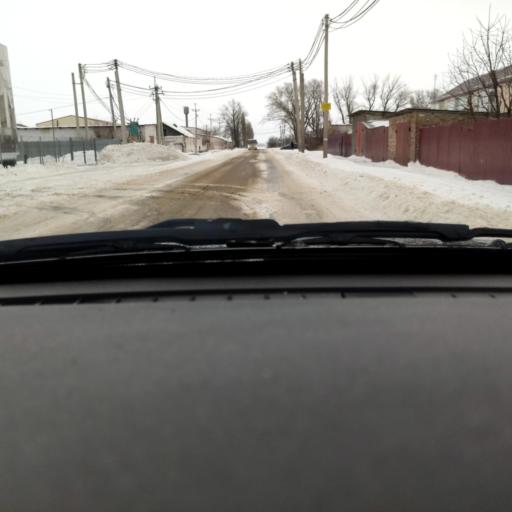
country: RU
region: Voronezj
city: Maslovka
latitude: 51.5383
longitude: 39.3420
